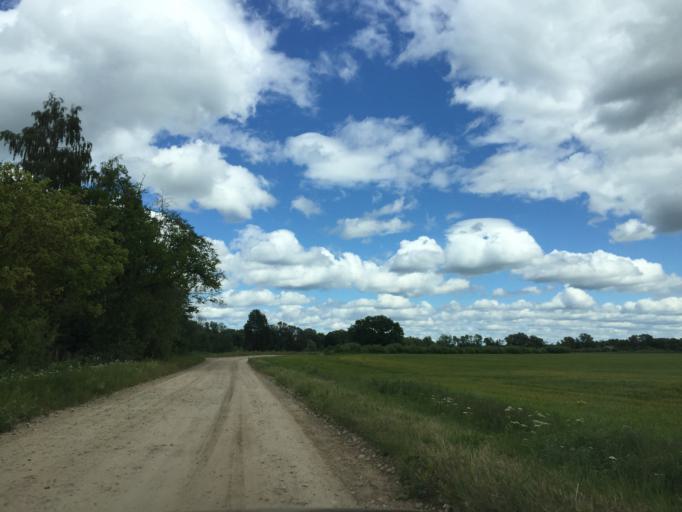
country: LV
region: Lecava
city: Iecava
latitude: 56.5878
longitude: 24.2398
